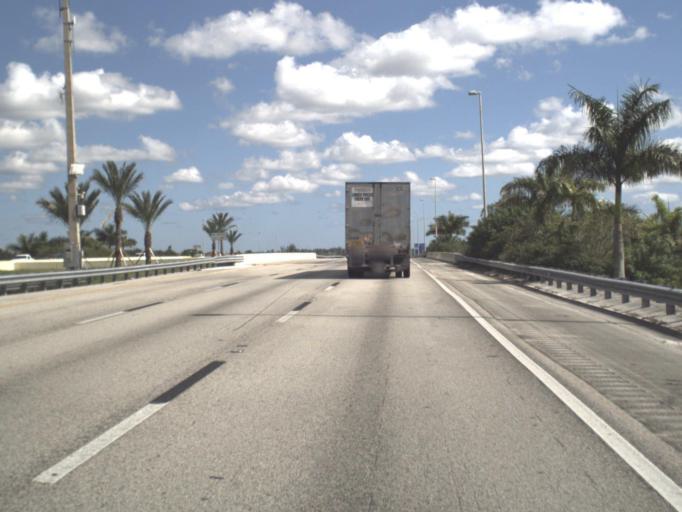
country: US
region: Florida
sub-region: Broward County
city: Coral Springs
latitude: 26.3021
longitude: -80.2800
